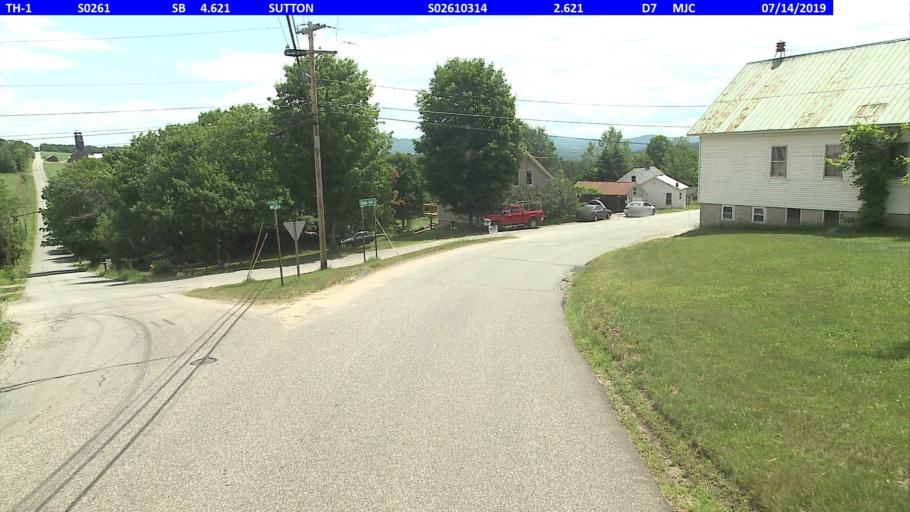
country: US
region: Vermont
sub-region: Caledonia County
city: Lyndonville
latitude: 44.6333
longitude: -72.0268
